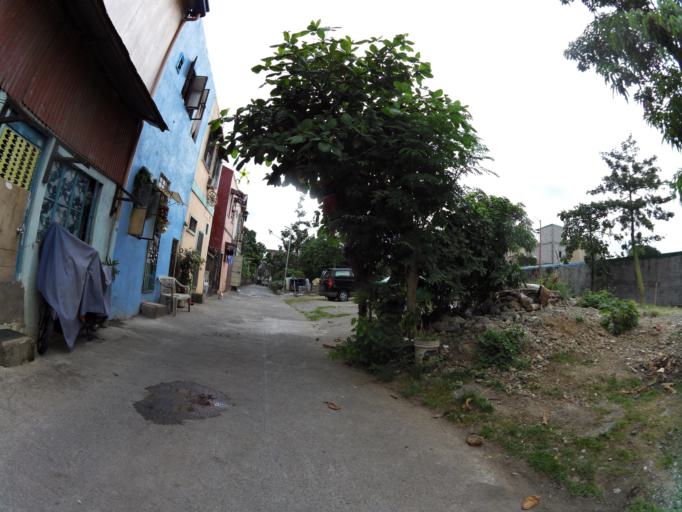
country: PH
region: Calabarzon
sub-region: Province of Rizal
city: Antipolo
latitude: 14.6401
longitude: 121.1120
